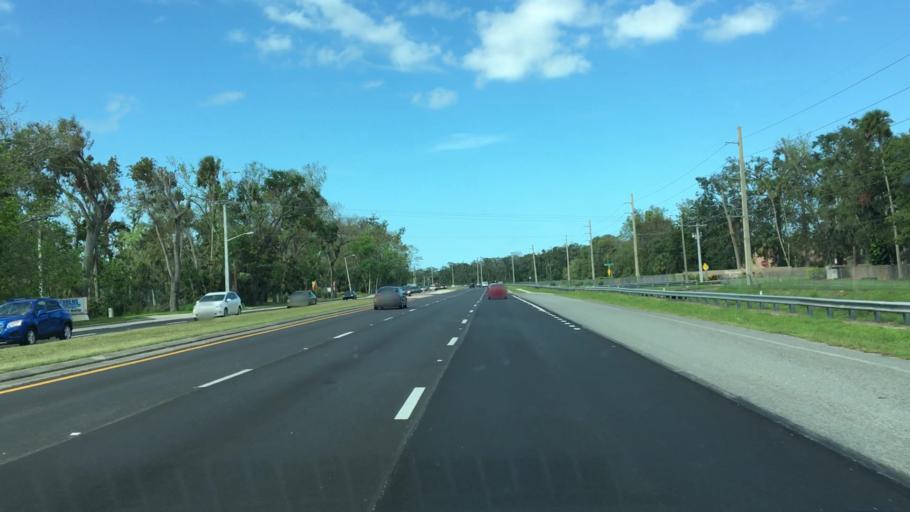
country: US
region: Florida
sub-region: Volusia County
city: Daytona Beach
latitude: 29.1829
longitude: -81.0297
